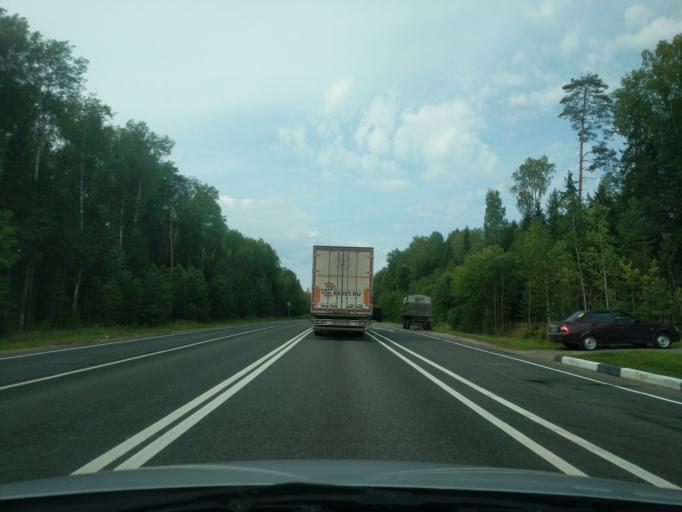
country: RU
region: Kirov
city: Leninskoye
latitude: 58.3190
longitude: 46.8671
